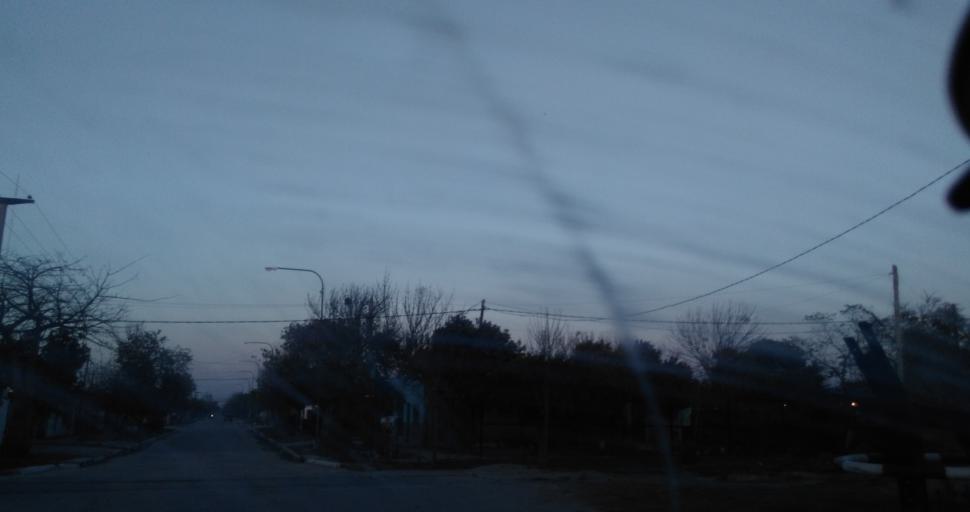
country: AR
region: Chaco
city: Resistencia
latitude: -27.4770
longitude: -58.9660
